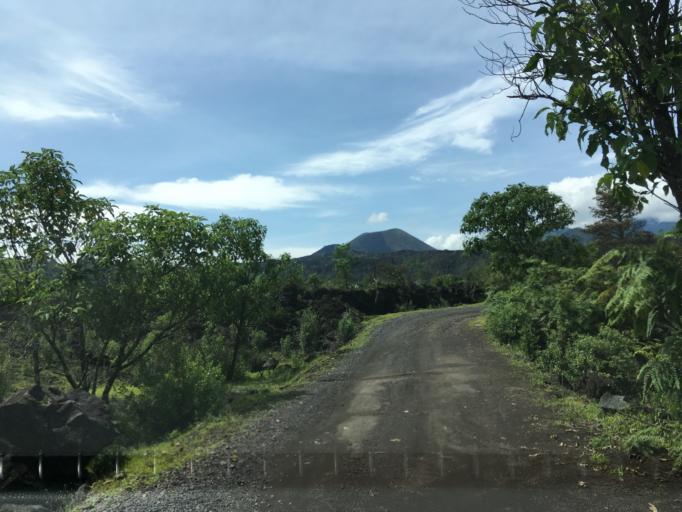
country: MX
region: Michoacan
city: Angahuan
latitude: 19.5315
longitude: -102.2499
